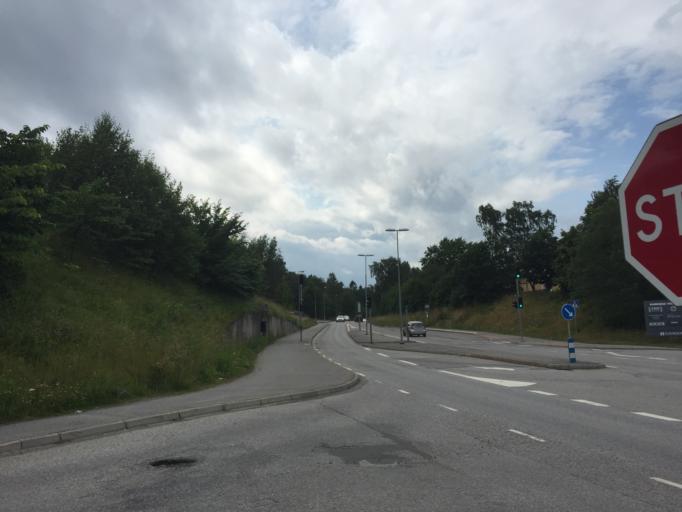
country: SE
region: Stockholm
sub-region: Botkyrka Kommun
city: Tullinge
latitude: 59.1995
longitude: 17.8835
